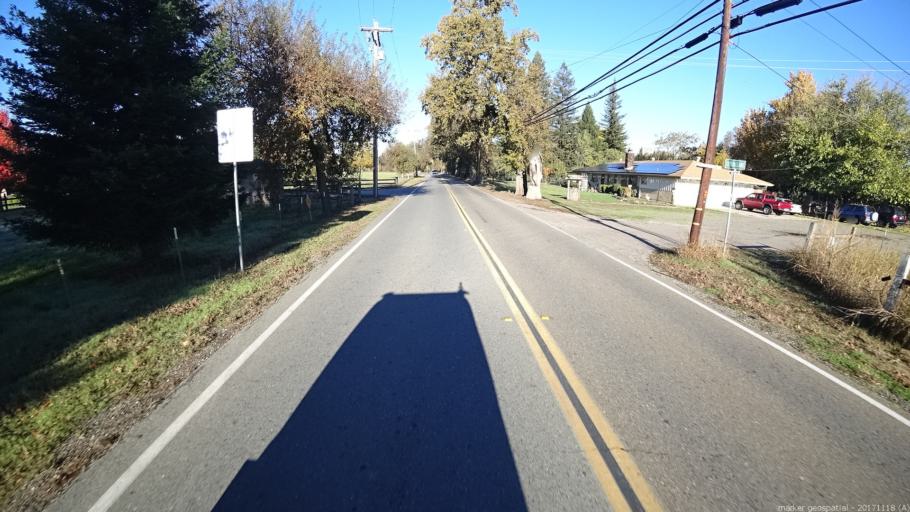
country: US
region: California
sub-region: Shasta County
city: Anderson
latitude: 40.4542
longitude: -122.2722
